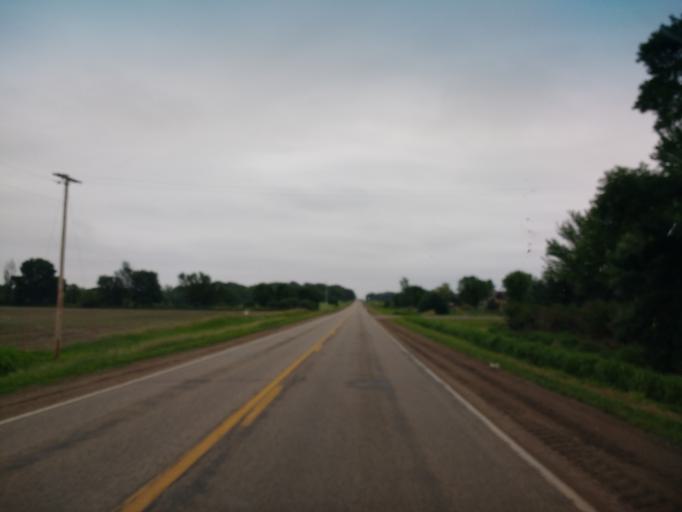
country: US
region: Iowa
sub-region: Dickinson County
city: Milford
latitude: 43.3278
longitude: -95.1260
